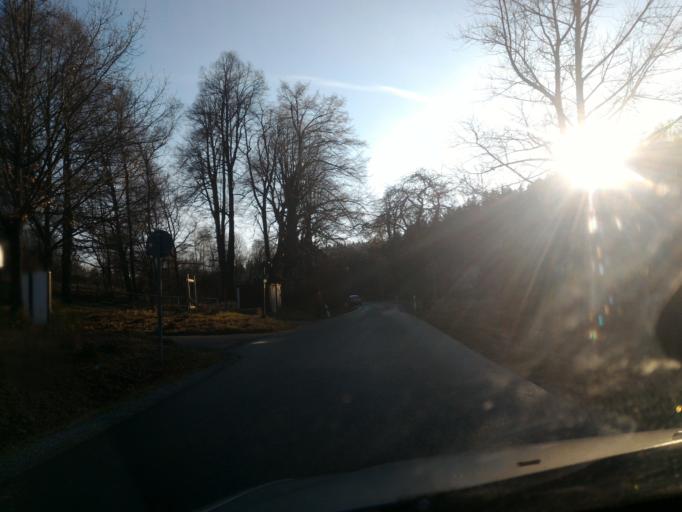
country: DE
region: Saxony
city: Kurort Jonsdorf
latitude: 50.8489
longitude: 14.7038
